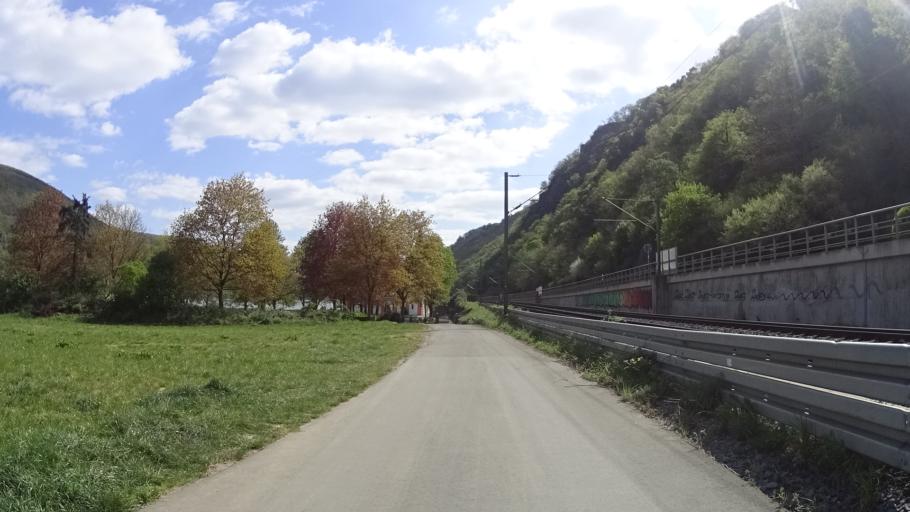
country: DE
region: Rheinland-Pfalz
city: Trechtingshausen
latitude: 50.0041
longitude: 7.8552
